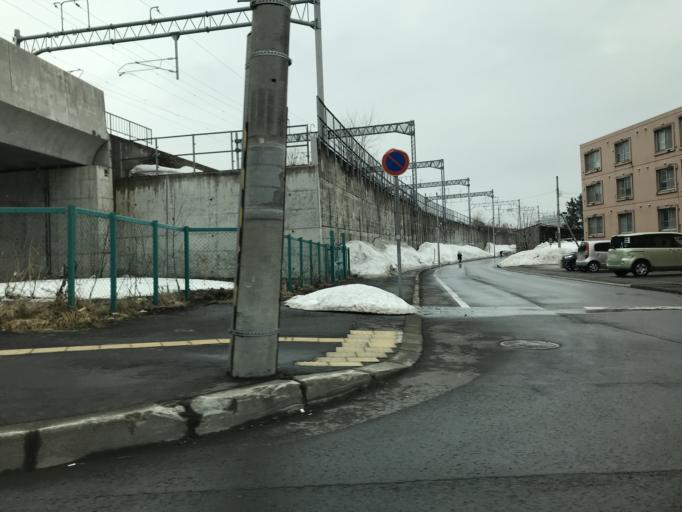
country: JP
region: Hokkaido
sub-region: Asahikawa-shi
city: Asahikawa
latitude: 43.7662
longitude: 142.3489
